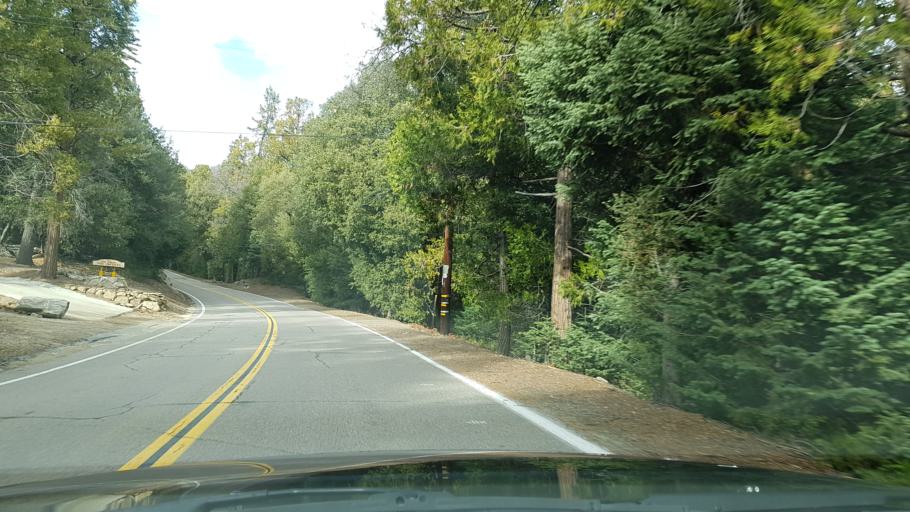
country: US
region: California
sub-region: Riverside County
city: Aguanga
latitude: 33.3383
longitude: -116.8746
